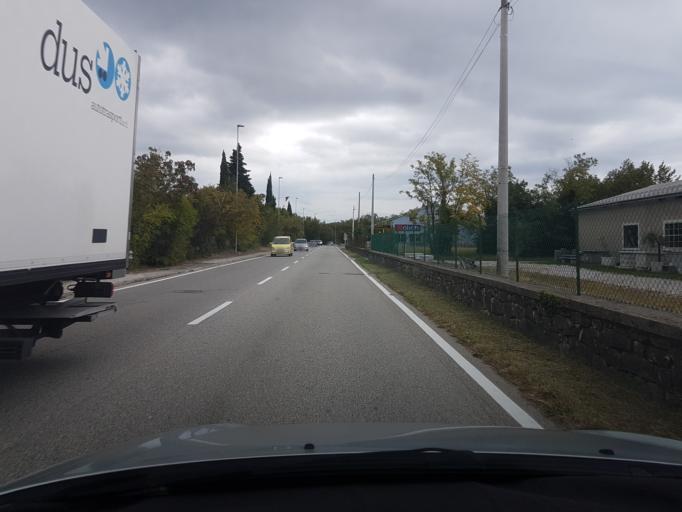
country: IT
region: Friuli Venezia Giulia
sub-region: Provincia di Trieste
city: Aurisina Cave
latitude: 45.7600
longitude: 13.6551
